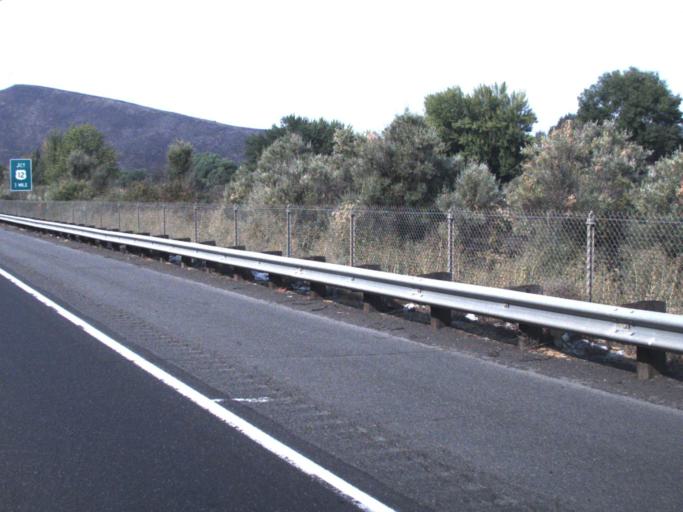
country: US
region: Washington
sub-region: Yakima County
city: Selah
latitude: 46.6418
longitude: -120.5159
